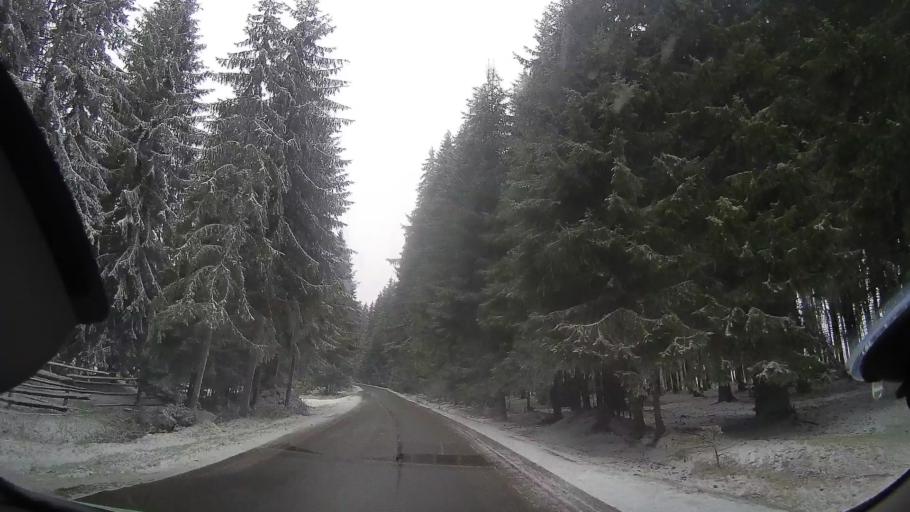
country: RO
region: Cluj
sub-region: Comuna Belis
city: Belis
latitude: 46.6440
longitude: 23.0596
